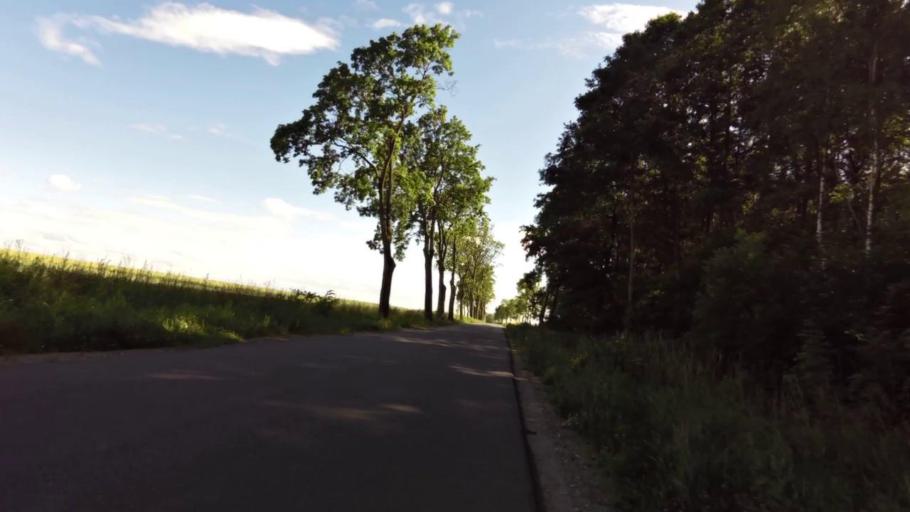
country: PL
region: West Pomeranian Voivodeship
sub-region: Powiat slawienski
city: Slawno
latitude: 54.4509
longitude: 16.7379
